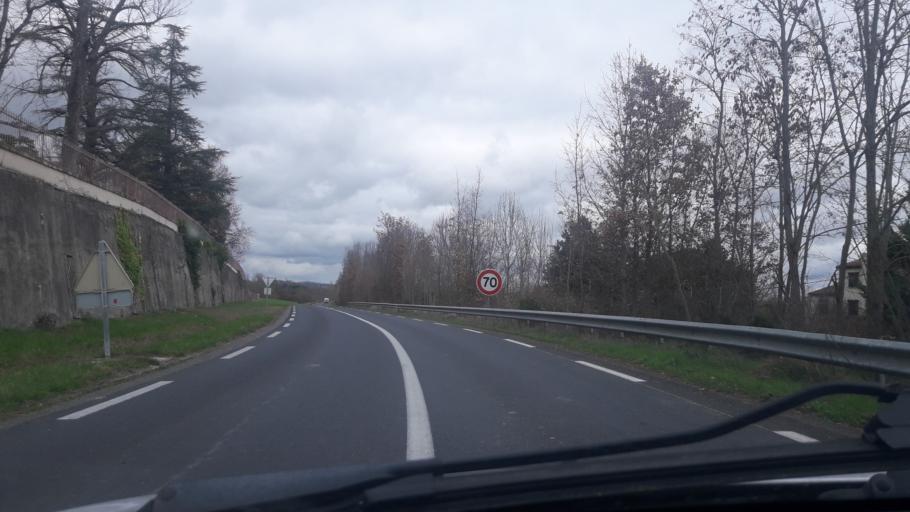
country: FR
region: Midi-Pyrenees
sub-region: Departement du Gers
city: Pujaudran
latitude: 43.6164
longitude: 1.0649
